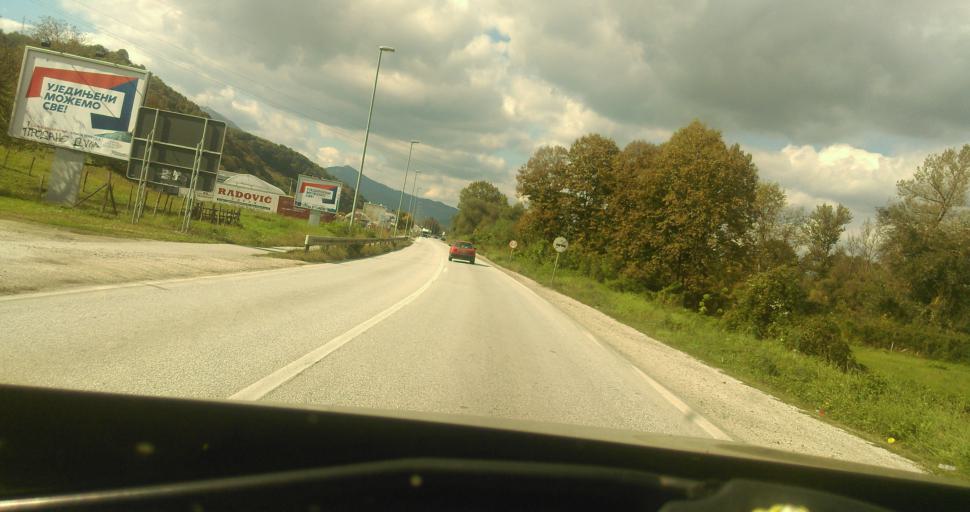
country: RS
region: Central Serbia
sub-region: Moravicki Okrug
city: Cacak
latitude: 43.8911
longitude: 20.3114
